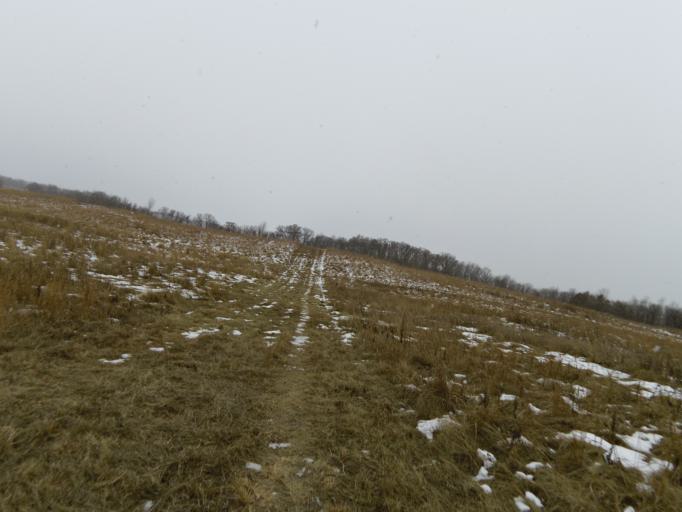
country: US
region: Minnesota
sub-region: Washington County
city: Lake Elmo
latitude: 44.9834
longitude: -92.9138
